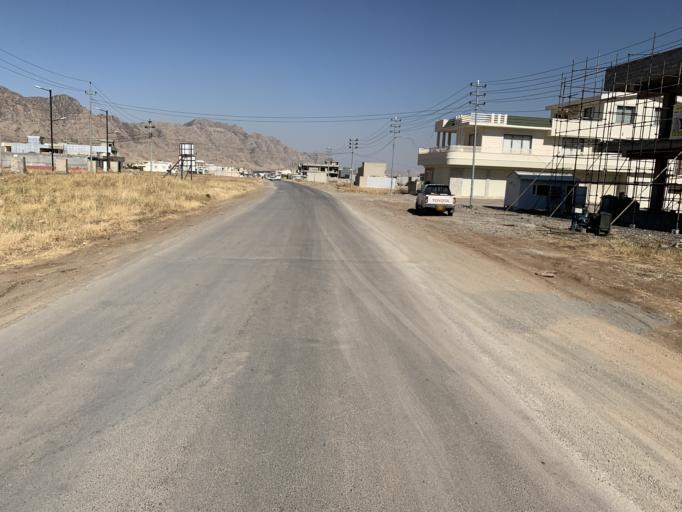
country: IQ
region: As Sulaymaniyah
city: Raniye
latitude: 36.2608
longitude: 44.8564
